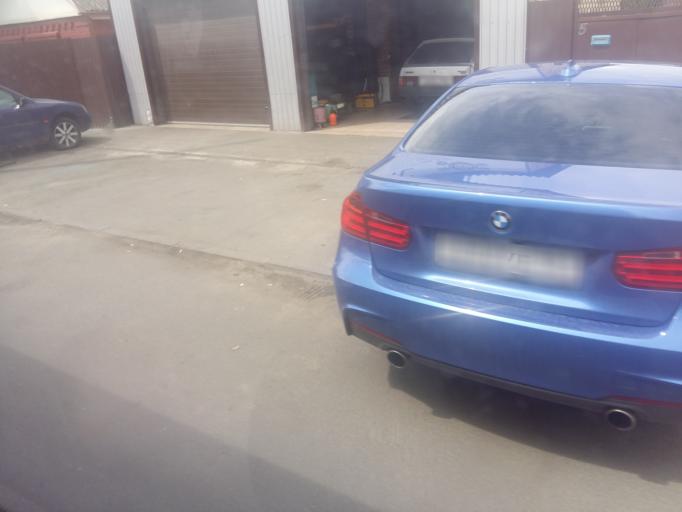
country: RU
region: Rostov
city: Imeni Chkalova
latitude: 47.2736
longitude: 39.7476
